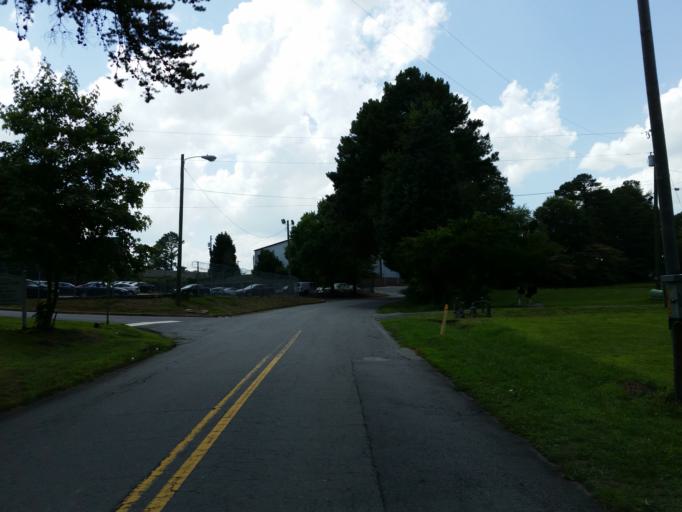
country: US
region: Georgia
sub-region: Cobb County
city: Fair Oaks
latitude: 33.9363
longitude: -84.5096
